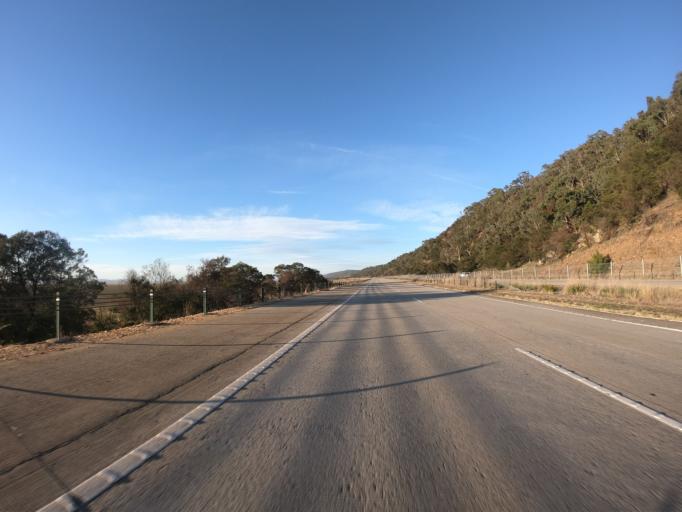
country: AU
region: New South Wales
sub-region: Yass Valley
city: Gundaroo
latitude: -35.0775
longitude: 149.3747
